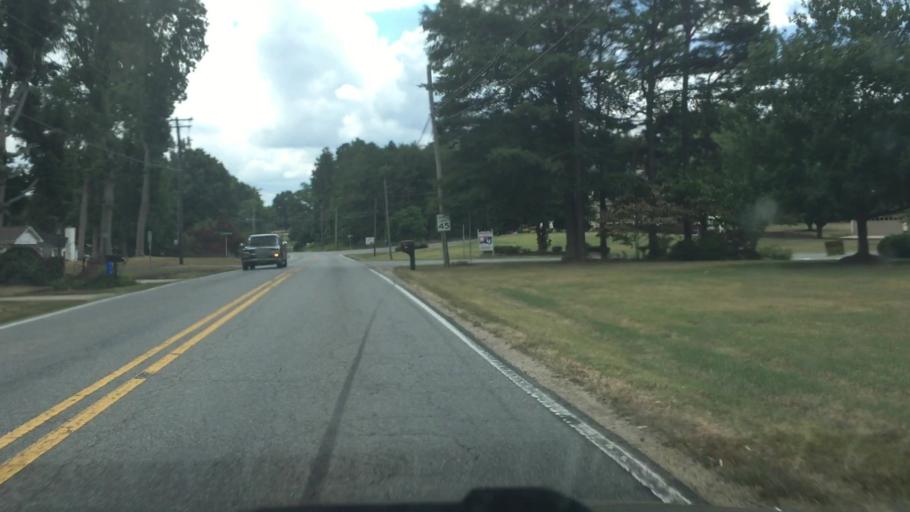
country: US
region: North Carolina
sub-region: Rowan County
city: Enochville
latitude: 35.5148
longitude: -80.6710
